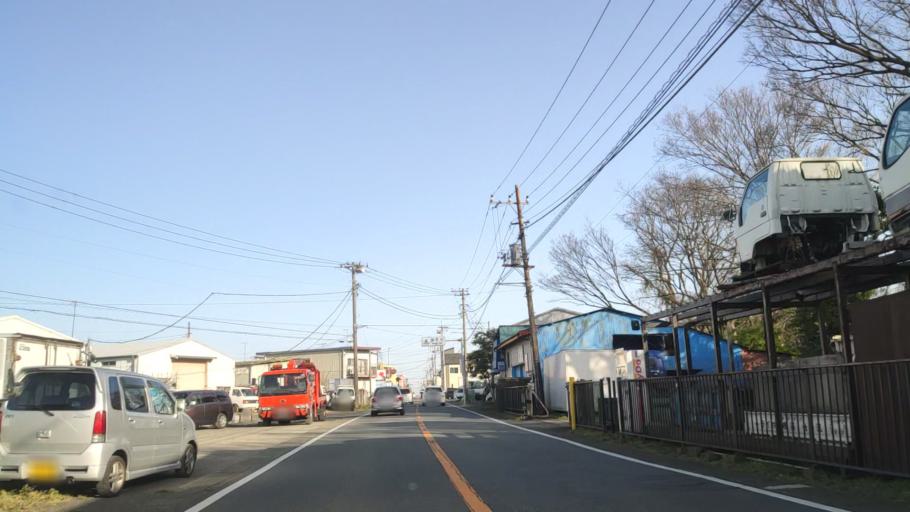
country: JP
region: Kanagawa
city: Zama
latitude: 35.5052
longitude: 139.3483
